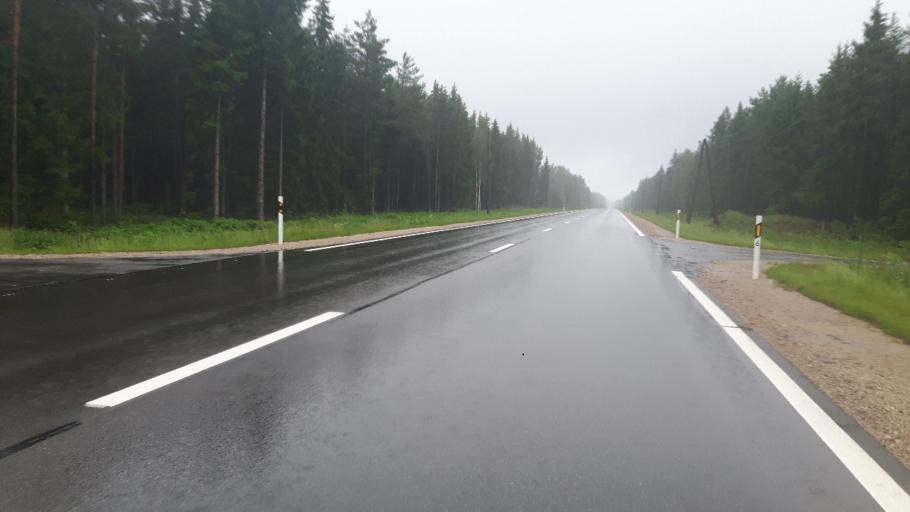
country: LV
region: Rucavas
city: Rucava
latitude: 56.1676
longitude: 21.1446
